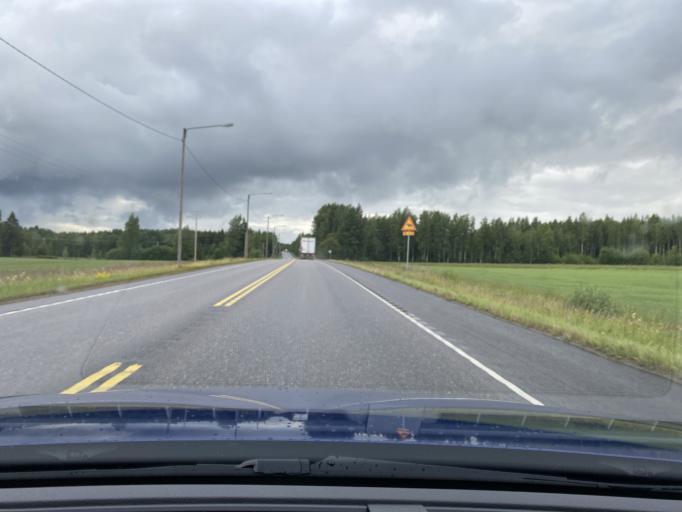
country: FI
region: Uusimaa
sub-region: Helsinki
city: Hyvinge
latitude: 60.5671
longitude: 24.8101
